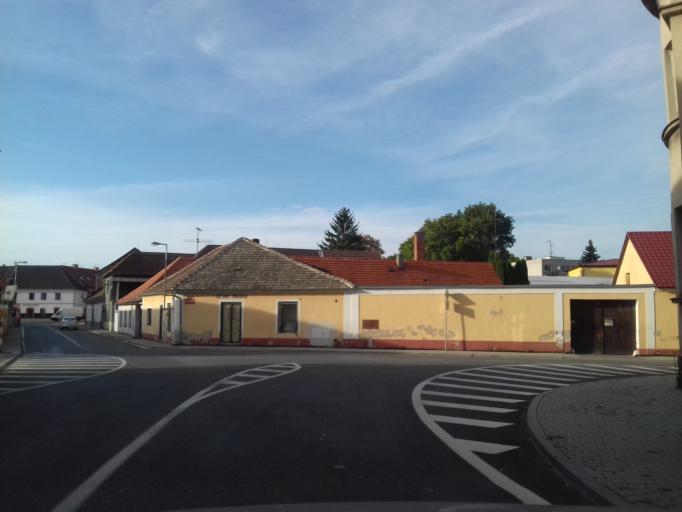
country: CZ
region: Central Bohemia
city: Neveklov
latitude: 49.7520
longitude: 14.5355
